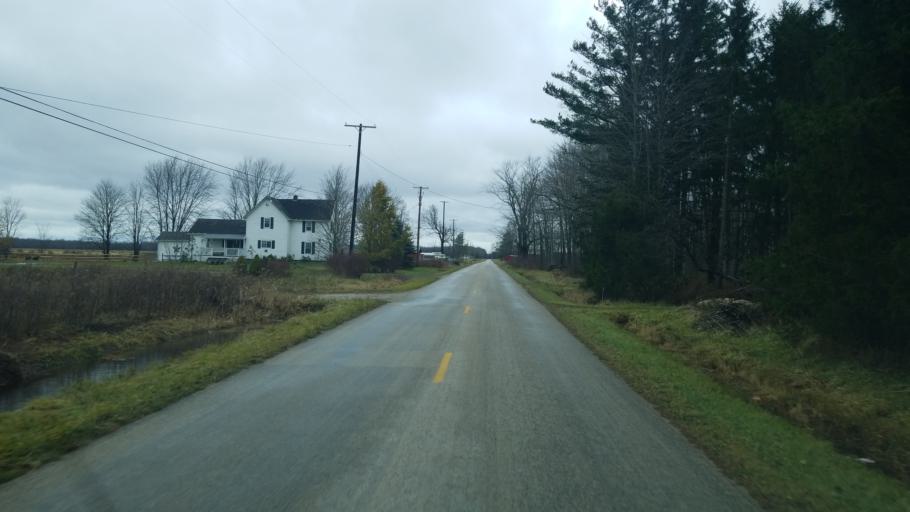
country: US
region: Ohio
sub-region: Ashtabula County
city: North Kingsville
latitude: 41.7991
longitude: -80.6240
